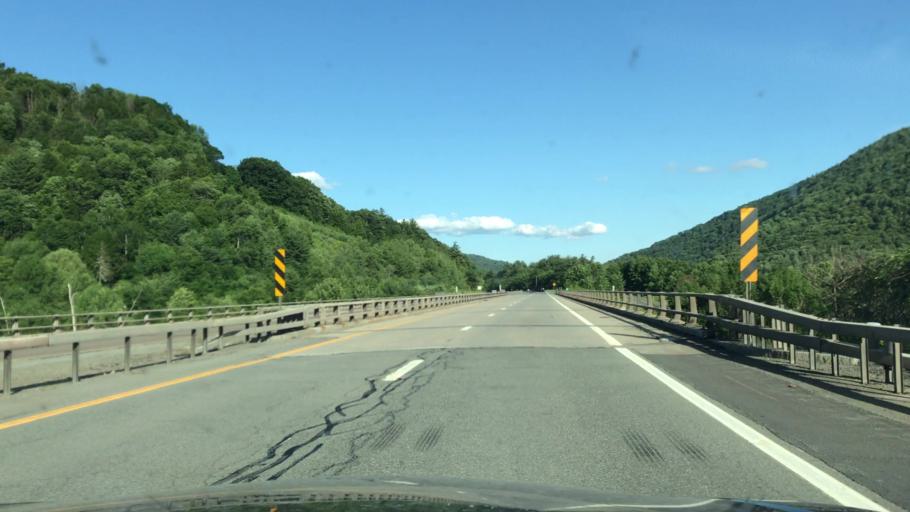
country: US
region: New York
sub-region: Delaware County
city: Hancock
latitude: 41.9919
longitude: -75.1307
